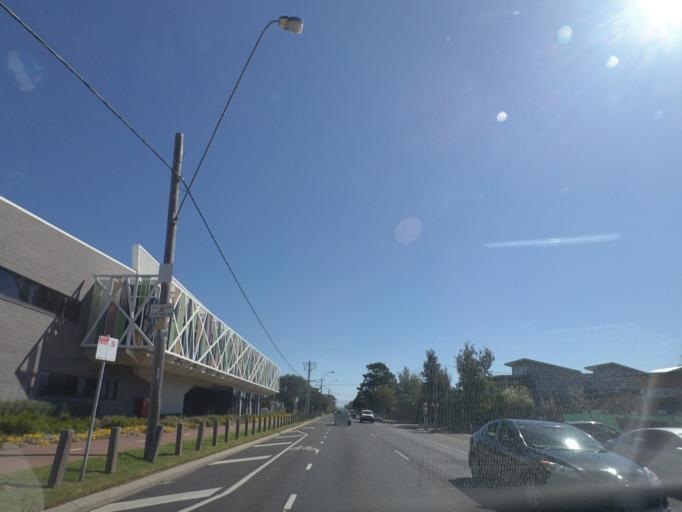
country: AU
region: Victoria
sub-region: Kingston
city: Edithvale
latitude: -38.0350
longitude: 145.1198
